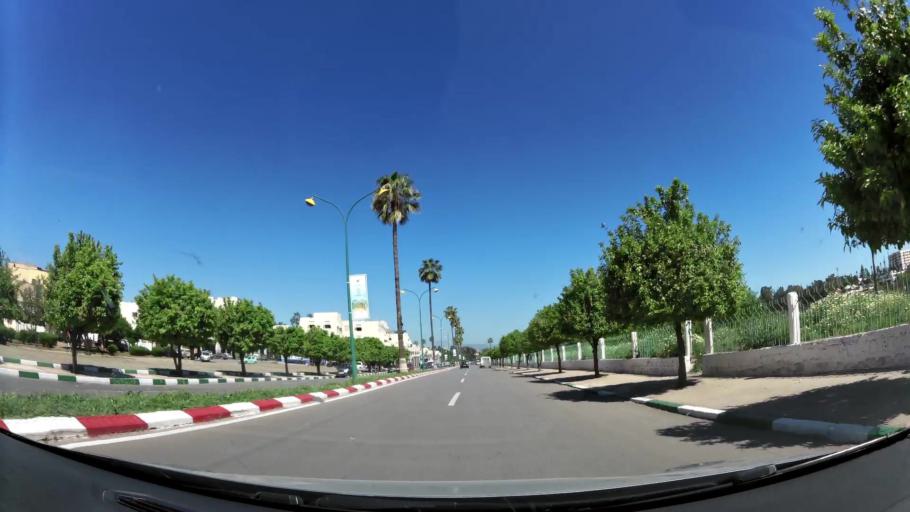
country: MA
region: Meknes-Tafilalet
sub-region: Meknes
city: Meknes
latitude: 33.8929
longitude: -5.5549
